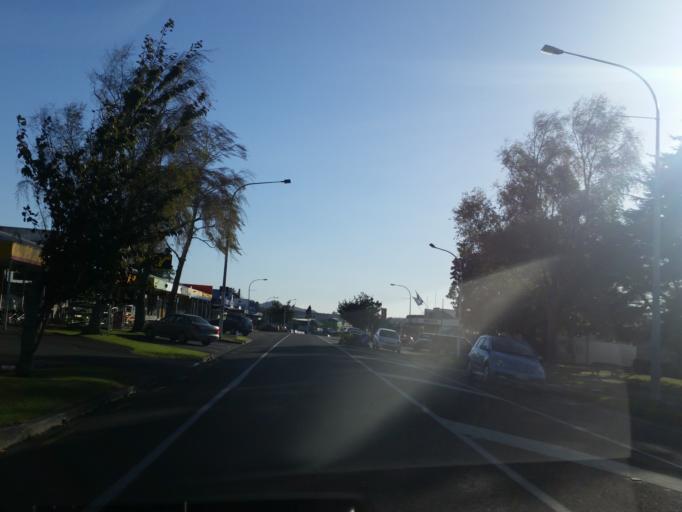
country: NZ
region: Bay of Plenty
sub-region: Western Bay of Plenty District
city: Katikati
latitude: -37.5556
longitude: 175.9169
